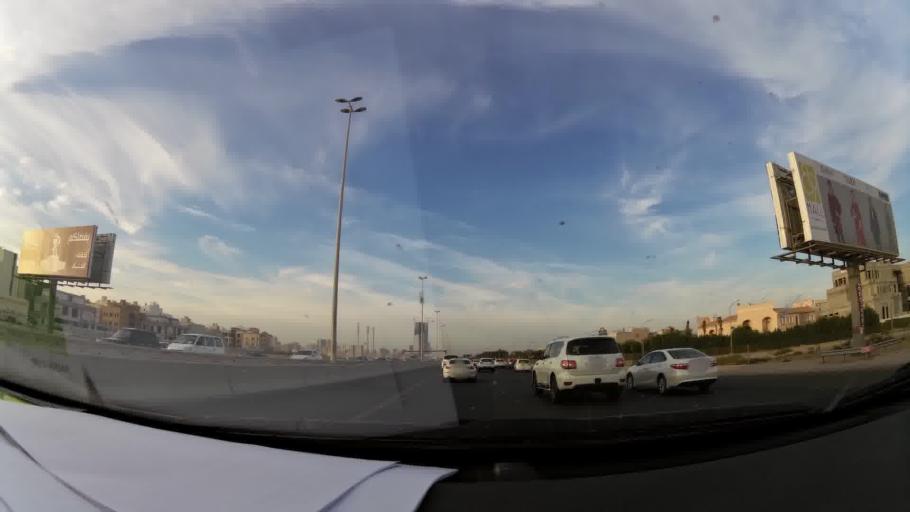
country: KW
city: Al Funaytis
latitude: 29.2365
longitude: 48.0958
